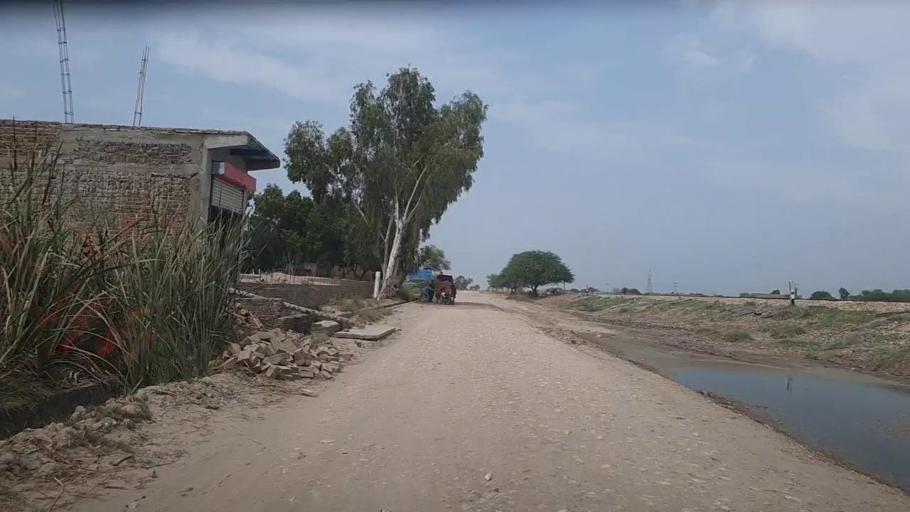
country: PK
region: Sindh
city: Bhiria
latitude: 26.8984
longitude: 68.2876
